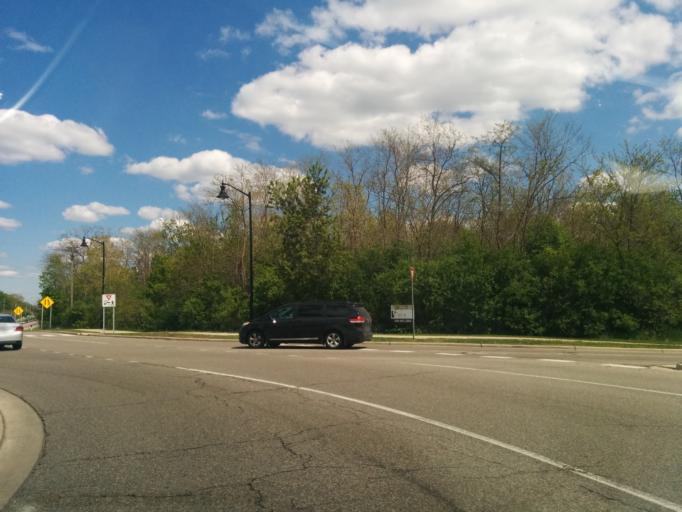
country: US
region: Michigan
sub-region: Oakland County
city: West Bloomfield Township
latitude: 42.5276
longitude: -83.3798
